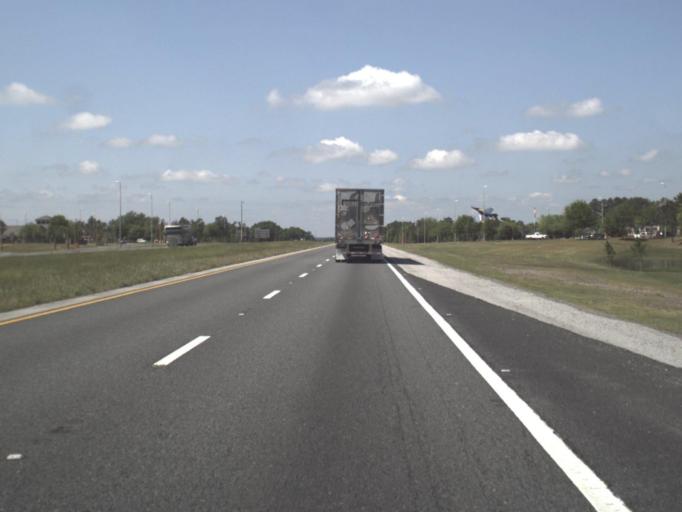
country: US
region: Florida
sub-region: Santa Rosa County
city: East Milton
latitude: 30.6132
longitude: -86.9755
